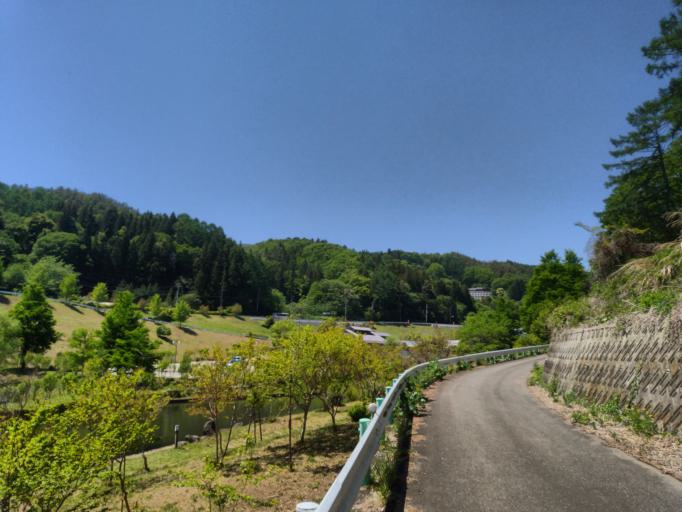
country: JP
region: Yamanashi
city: Nirasaki
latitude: 35.8645
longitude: 138.4292
